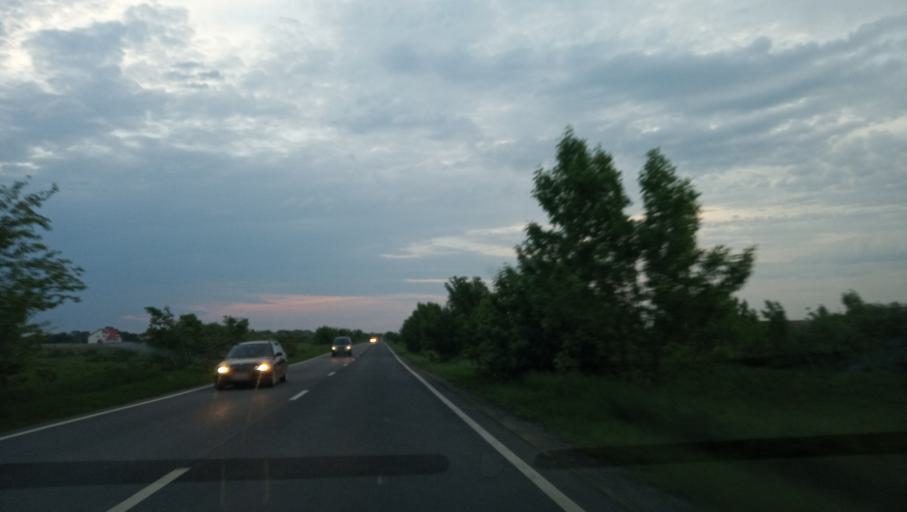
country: RO
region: Timis
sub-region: Comuna Jebel
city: Jebel
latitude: 45.5458
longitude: 21.2245
